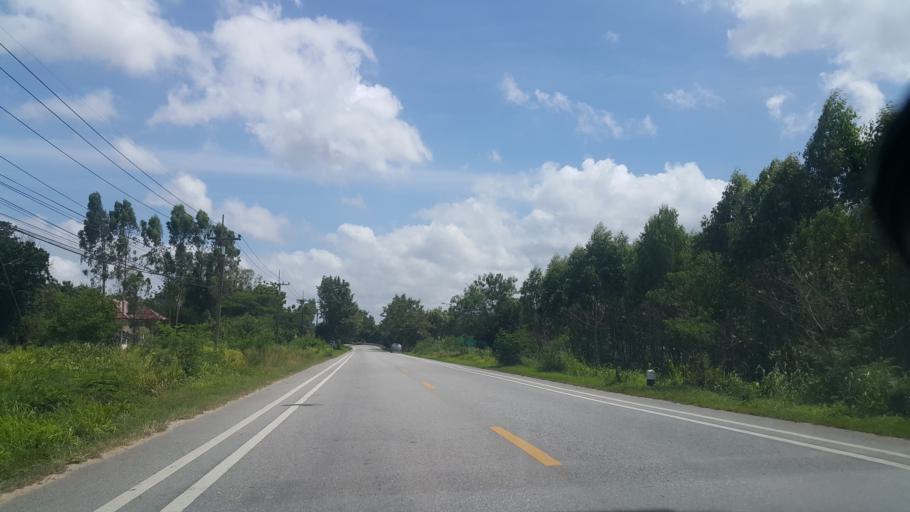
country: TH
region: Rayong
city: Ban Chang
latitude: 12.8044
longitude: 101.0531
